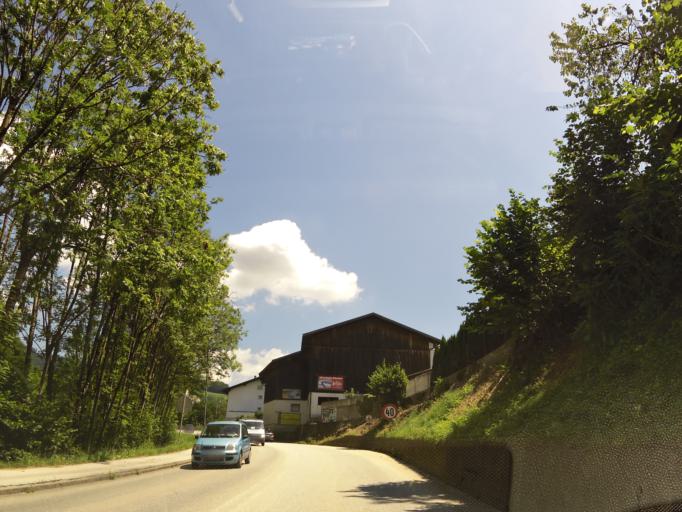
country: AT
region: Tyrol
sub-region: Politischer Bezirk Kufstein
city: Niederndorf
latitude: 47.6493
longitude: 12.2105
